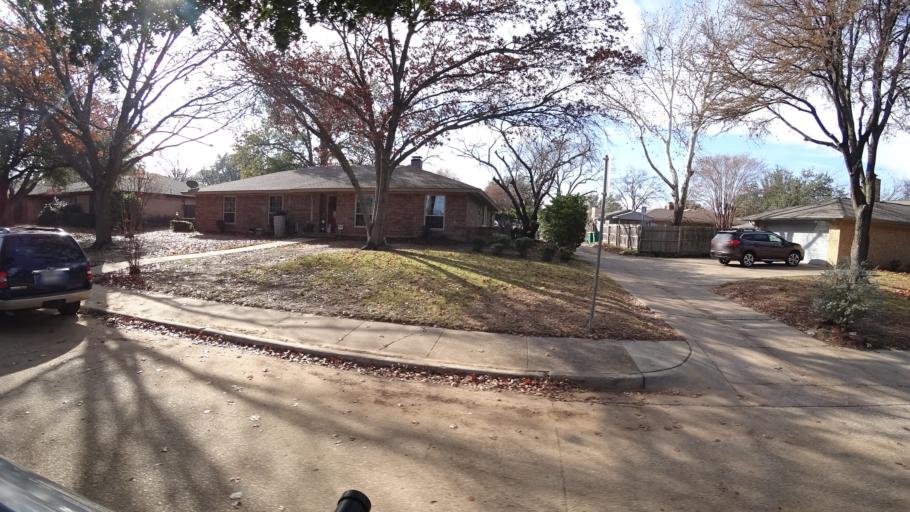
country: US
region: Texas
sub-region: Denton County
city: Lewisville
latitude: 33.0503
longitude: -97.0254
